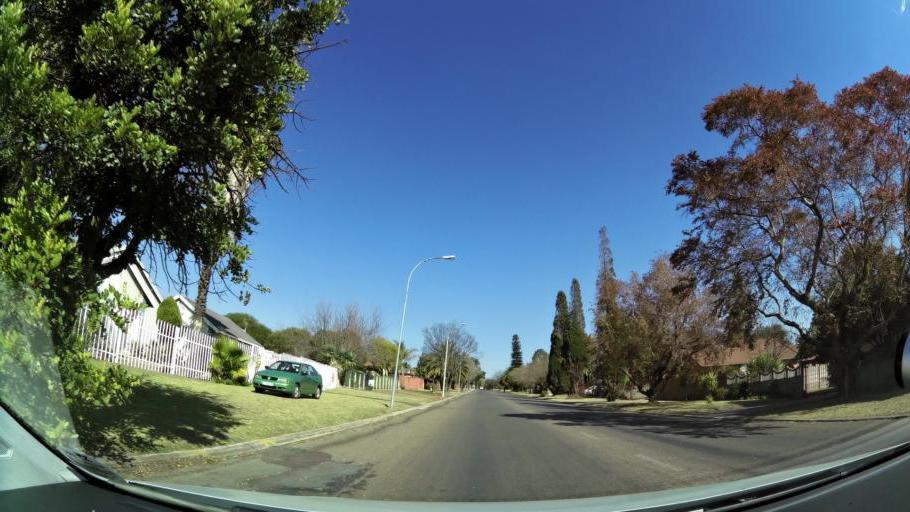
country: ZA
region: Gauteng
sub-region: Ekurhuleni Metropolitan Municipality
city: Tembisa
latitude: -26.0434
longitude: 28.2376
